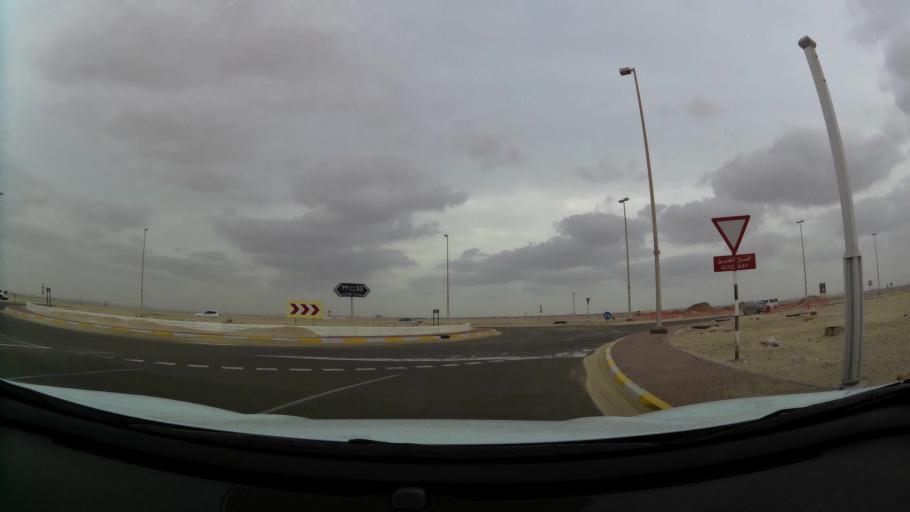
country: AE
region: Abu Dhabi
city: Abu Dhabi
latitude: 24.3690
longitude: 54.6239
